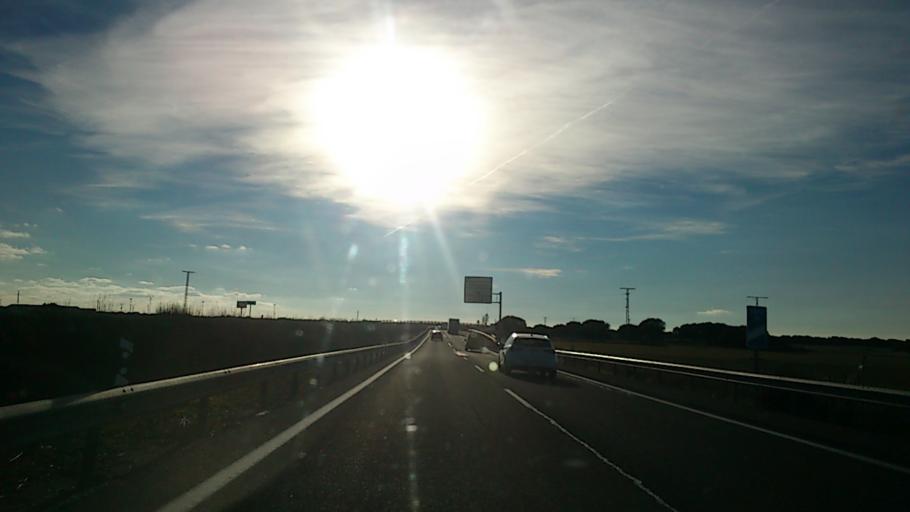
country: ES
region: Castille-La Mancha
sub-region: Provincia de Guadalajara
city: Mirabueno
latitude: 40.9339
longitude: -2.7089
